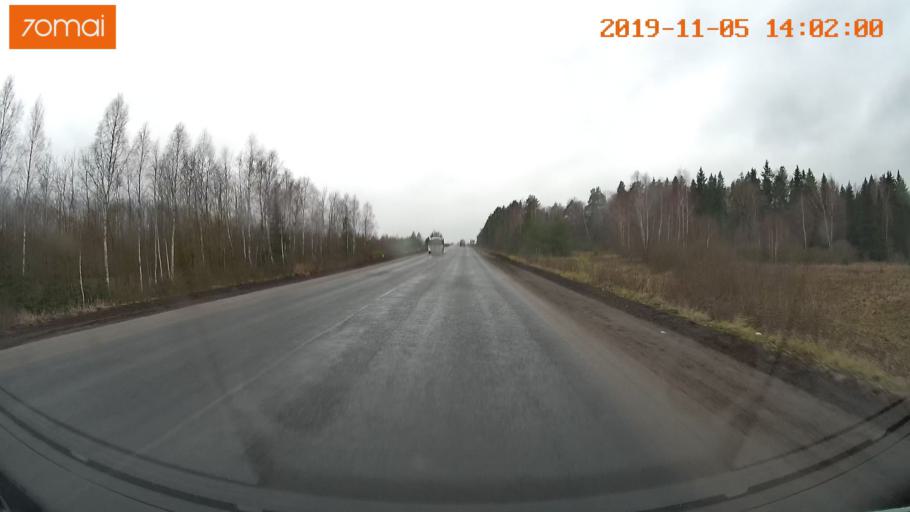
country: RU
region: Ivanovo
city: Kokhma
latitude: 57.0051
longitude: 41.2214
